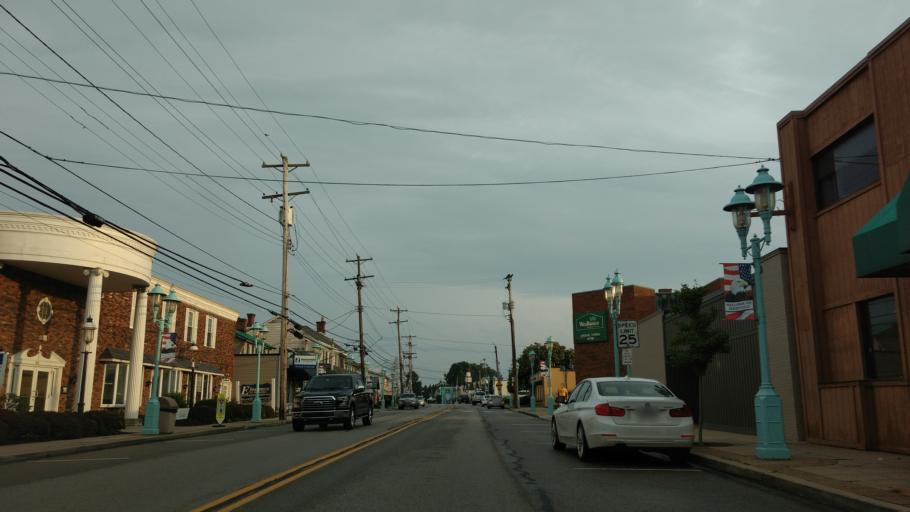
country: US
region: Pennsylvania
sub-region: Allegheny County
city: West View
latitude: 40.5404
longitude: -80.0362
